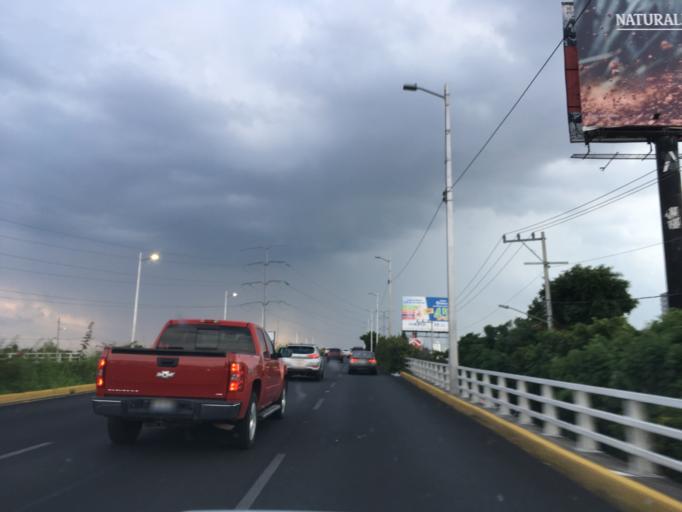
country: MX
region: Jalisco
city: Guadalajara
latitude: 20.6746
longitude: -103.3975
